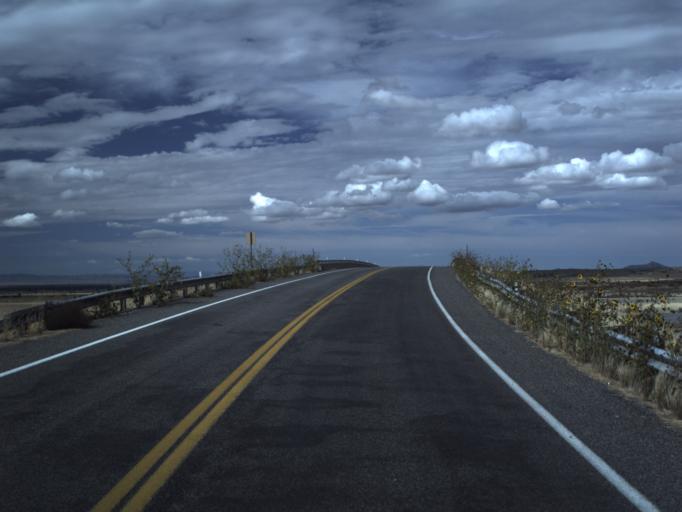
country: US
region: Utah
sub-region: Millard County
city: Fillmore
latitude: 38.9778
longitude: -112.3372
